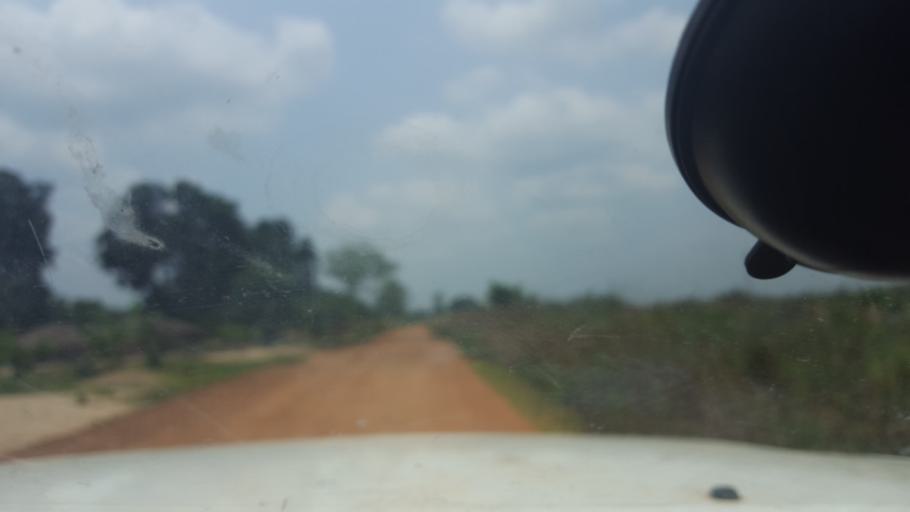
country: CD
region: Bandundu
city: Bandundu
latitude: -3.3336
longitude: 17.2839
